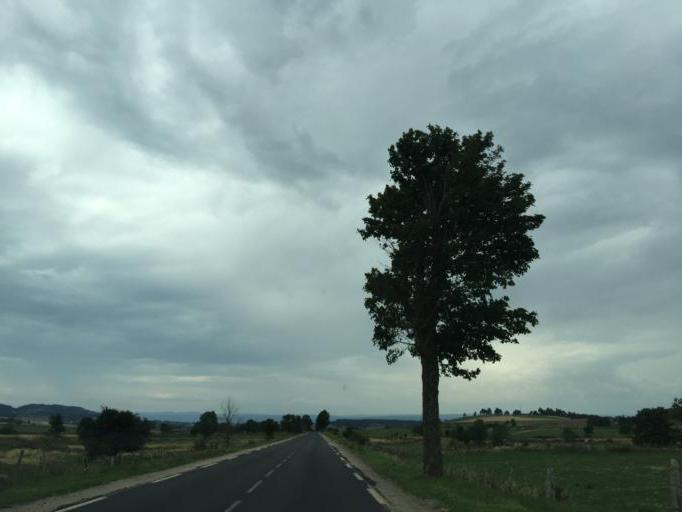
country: FR
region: Auvergne
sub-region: Departement de la Haute-Loire
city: Solignac-sur-Loire
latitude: 44.8546
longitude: 3.8417
